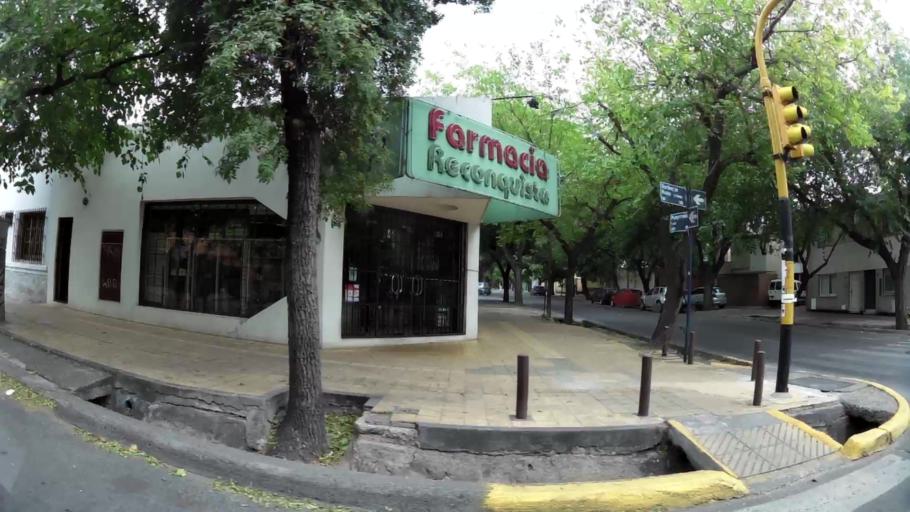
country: AR
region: Mendoza
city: Mendoza
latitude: -32.8995
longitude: -68.8571
